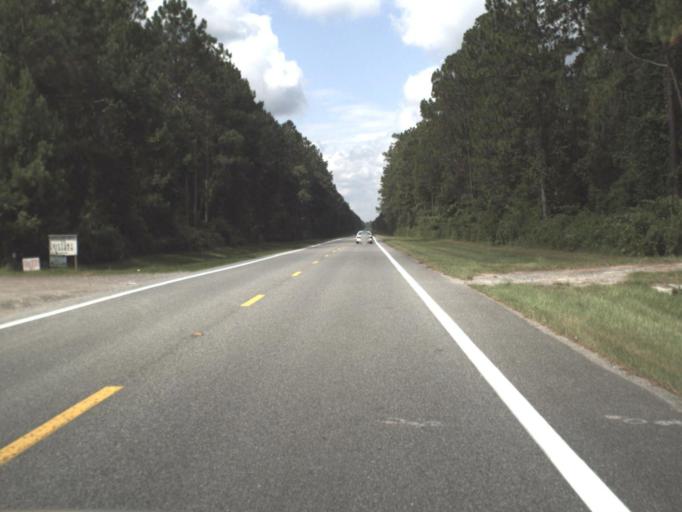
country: US
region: Florida
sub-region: Baker County
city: Macclenny
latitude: 30.1402
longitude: -82.1889
